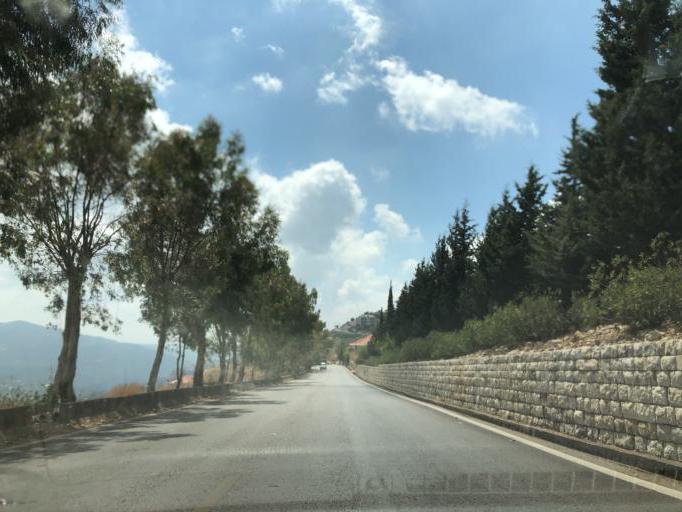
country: LB
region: Mont-Liban
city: Beit ed Dine
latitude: 33.6949
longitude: 35.5449
